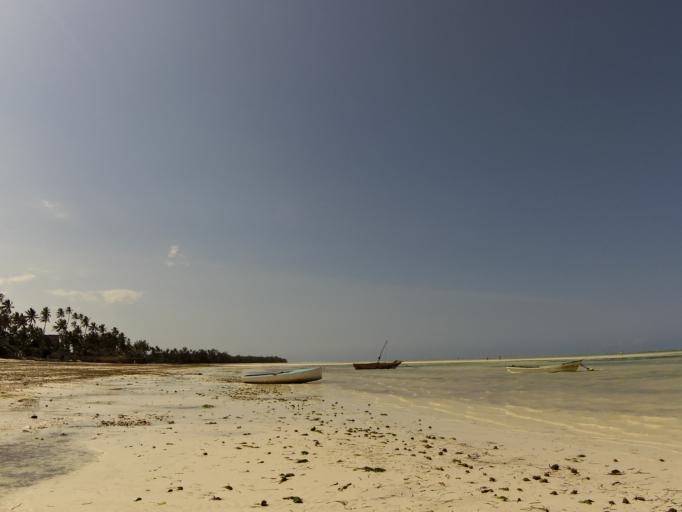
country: TZ
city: Kiwengwa
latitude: -6.0906
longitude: 39.4261
